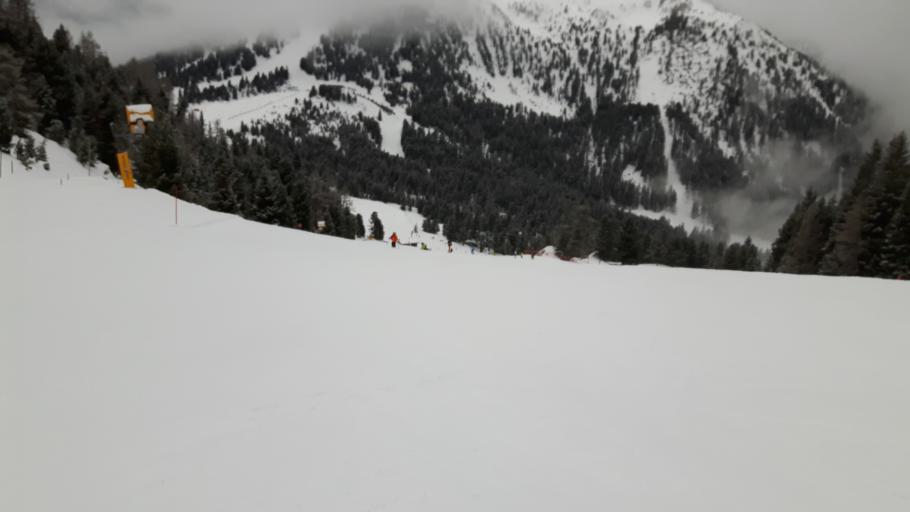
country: IT
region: Trentino-Alto Adige
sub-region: Bolzano
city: Nova Levante
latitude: 46.3613
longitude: 11.5446
